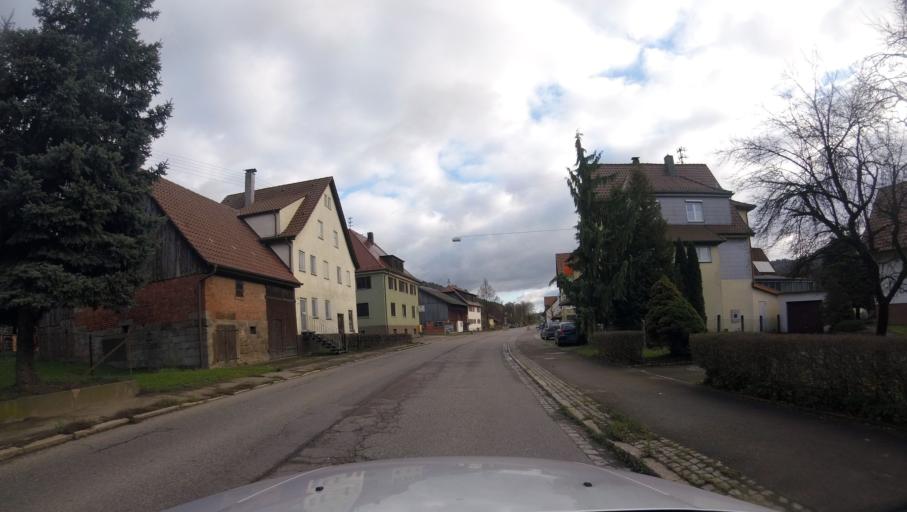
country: DE
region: Baden-Wuerttemberg
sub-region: Regierungsbezirk Stuttgart
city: Sulzbach an der Murr
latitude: 48.9975
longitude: 9.5319
